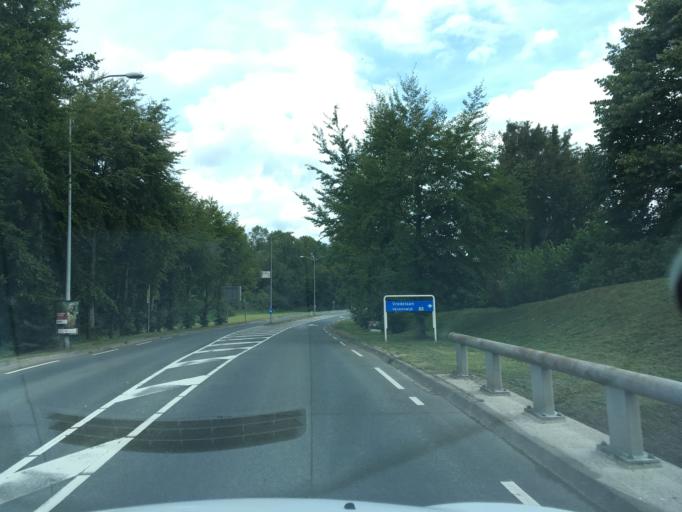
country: NL
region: Flevoland
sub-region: Gemeente Almere
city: Almere Stad
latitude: 52.3786
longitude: 5.2343
